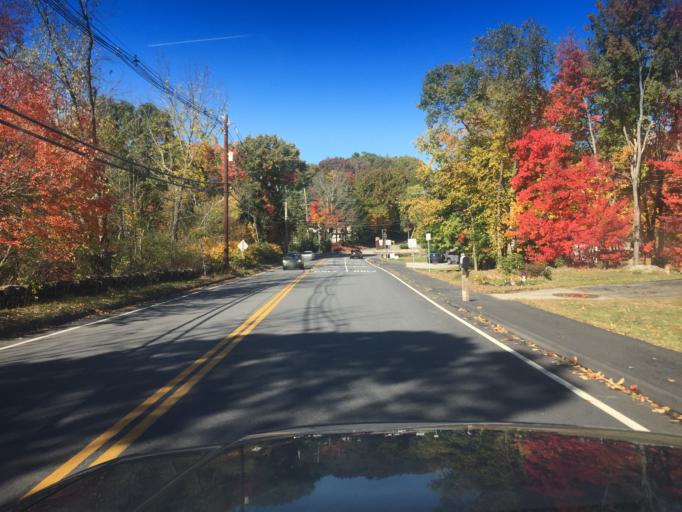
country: US
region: Massachusetts
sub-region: Middlesex County
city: Hudson
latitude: 42.3867
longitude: -71.5490
